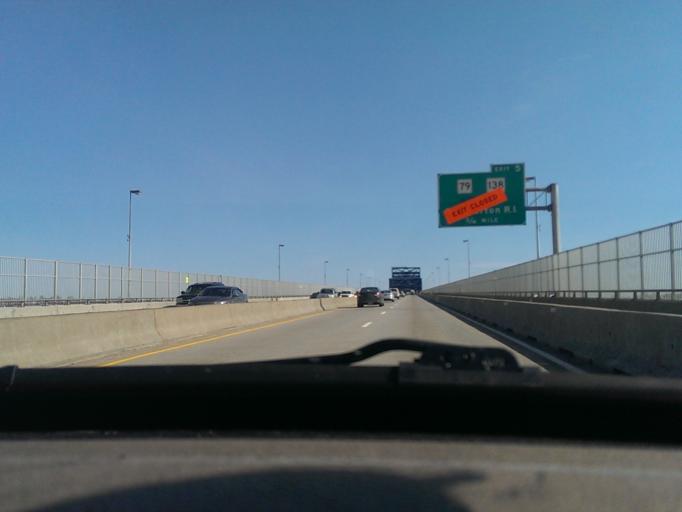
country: US
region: Massachusetts
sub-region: Bristol County
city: Fall River
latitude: 41.7111
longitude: -71.1734
